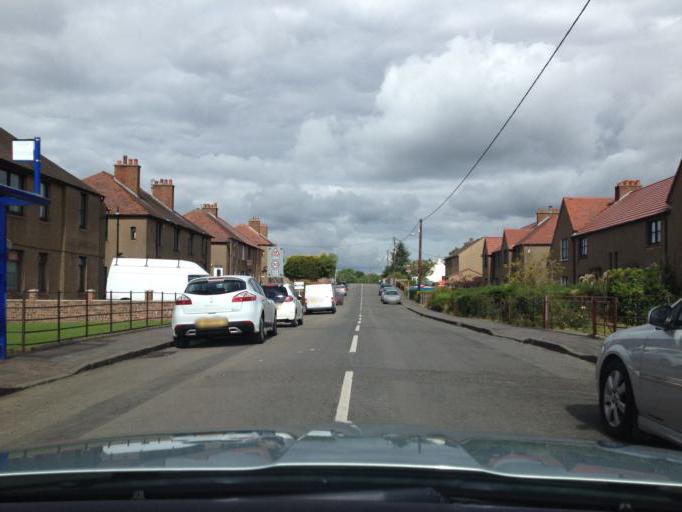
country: GB
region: Scotland
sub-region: Falkirk
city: Falkirk
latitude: 55.9651
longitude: -3.7523
